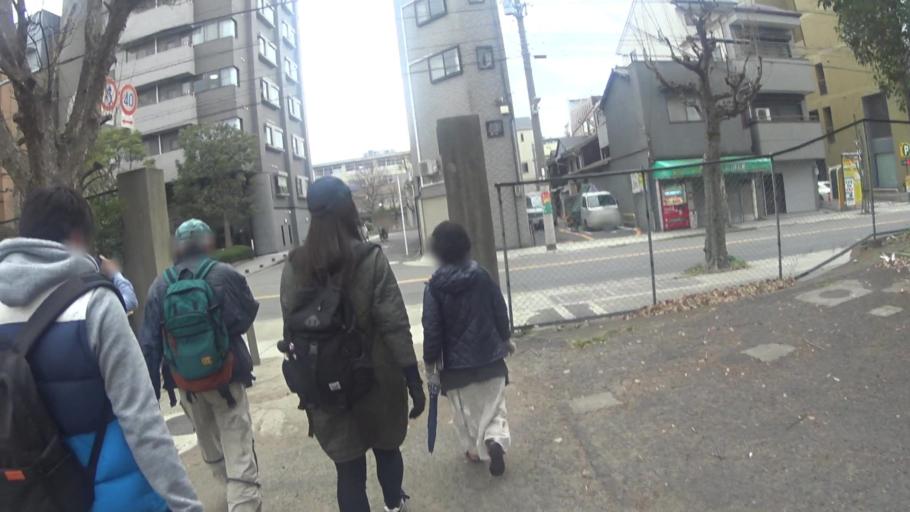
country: JP
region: Osaka
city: Osaka-shi
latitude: 34.6786
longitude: 135.5228
